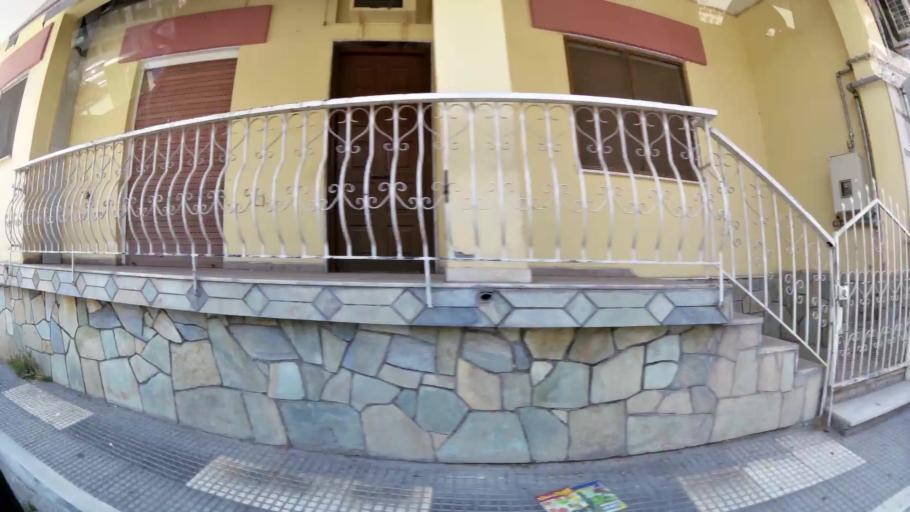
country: GR
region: Central Macedonia
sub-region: Nomos Thessalonikis
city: Diavata
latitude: 40.6883
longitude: 22.8588
